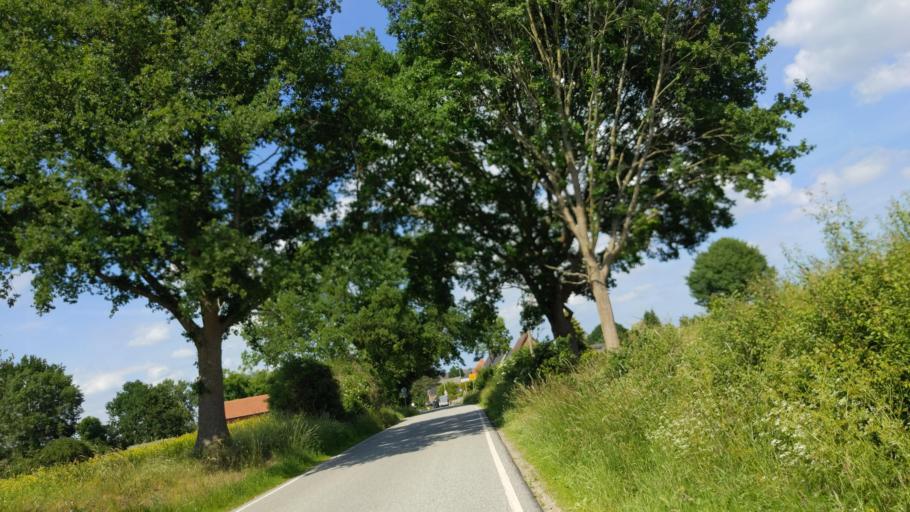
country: DE
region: Schleswig-Holstein
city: Krummesse
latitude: 53.8072
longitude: 10.6813
